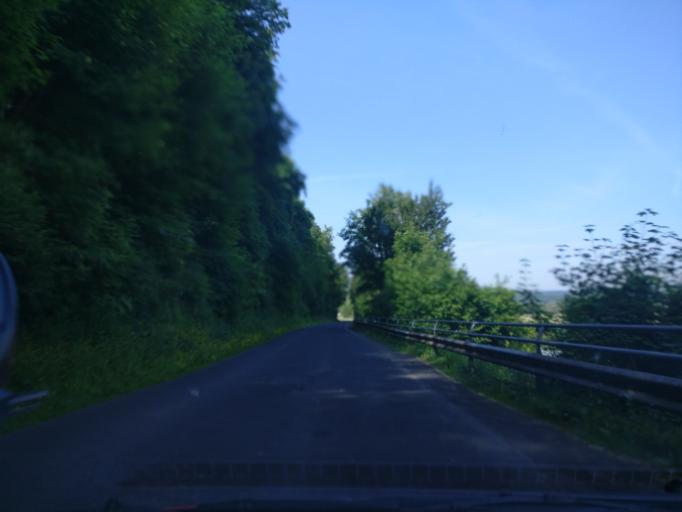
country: DE
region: Lower Saxony
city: Scheden
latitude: 51.3856
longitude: 9.7618
